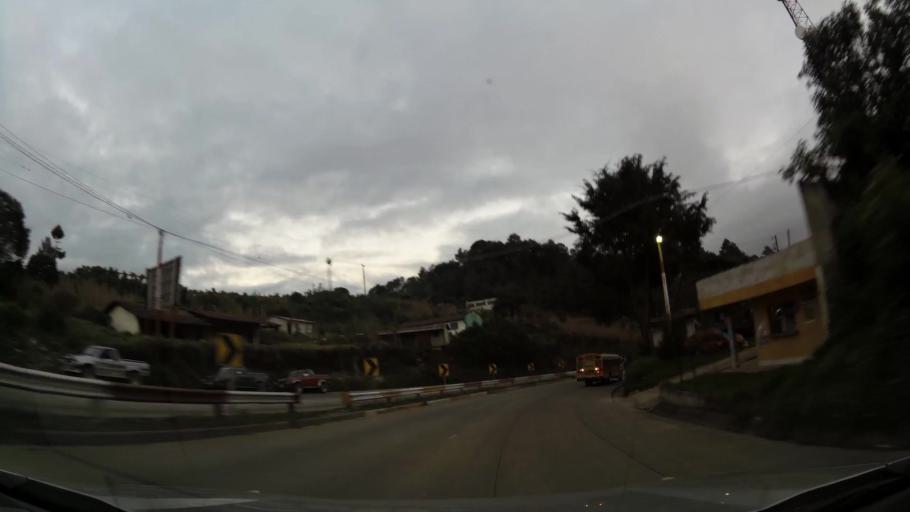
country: GT
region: Quiche
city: Chichicastenango
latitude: 14.8600
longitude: -91.0579
